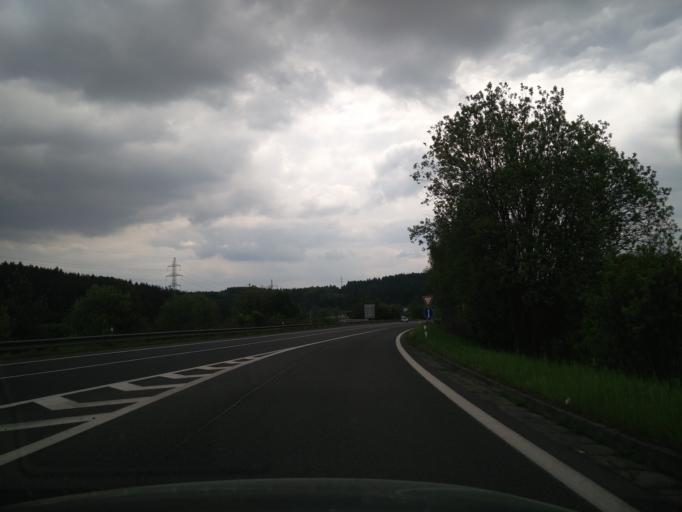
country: CZ
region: Central Bohemia
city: Milin
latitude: 49.6368
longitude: 14.0510
